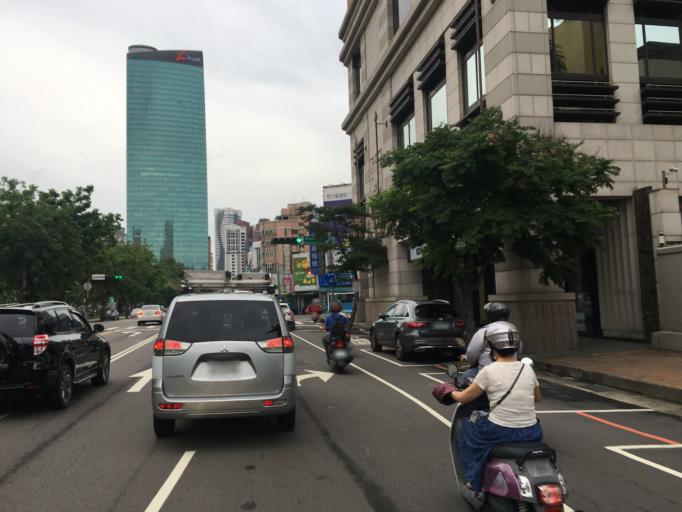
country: TW
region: Taiwan
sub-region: Taichung City
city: Taichung
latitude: 24.1462
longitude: 120.6654
